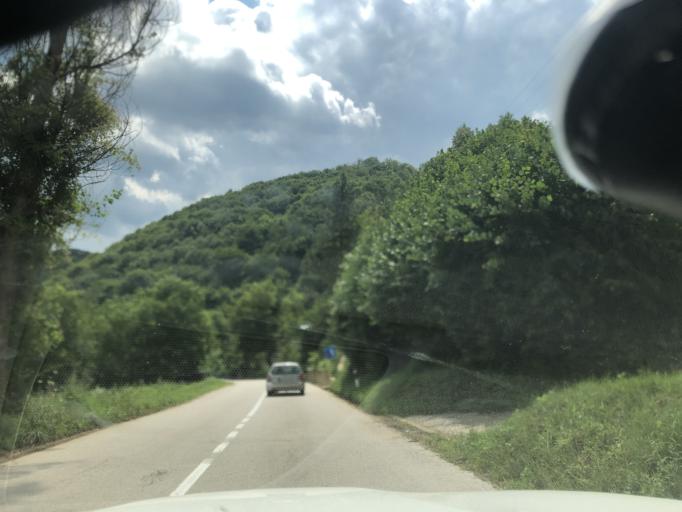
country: RS
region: Central Serbia
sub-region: Jablanicki Okrug
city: Medvega
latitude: 42.7892
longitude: 21.5828
